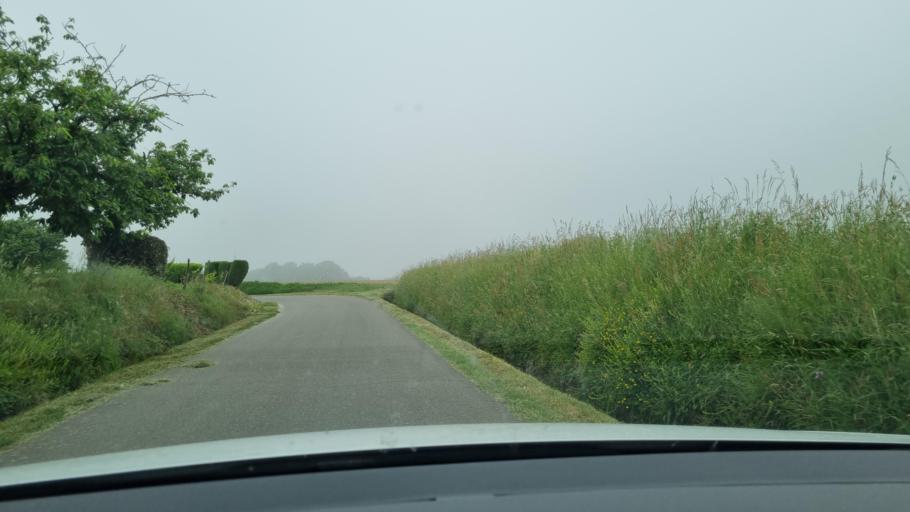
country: FR
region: Aquitaine
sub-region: Departement des Landes
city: Hagetmau
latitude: 43.6480
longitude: -0.6084
